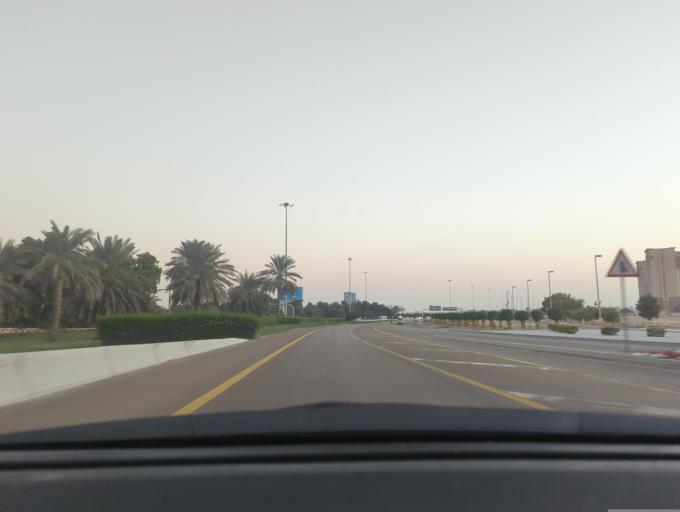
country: AE
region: Abu Dhabi
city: Abu Dhabi
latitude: 24.3912
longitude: 54.5229
